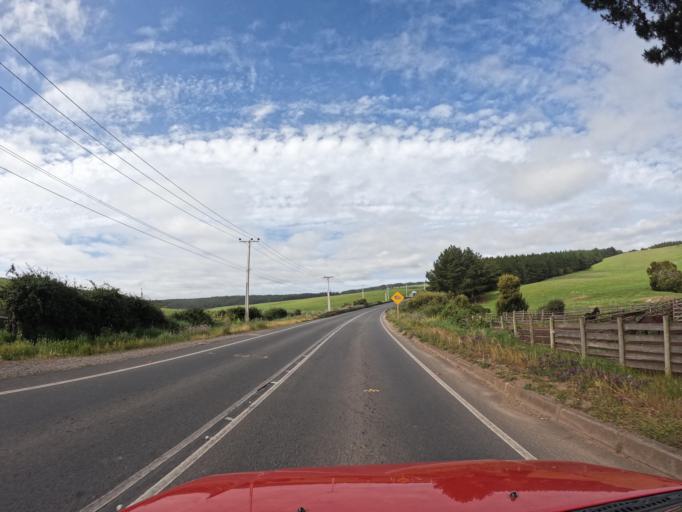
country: CL
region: O'Higgins
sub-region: Provincia de Colchagua
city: Santa Cruz
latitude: -34.3503
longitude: -71.9382
